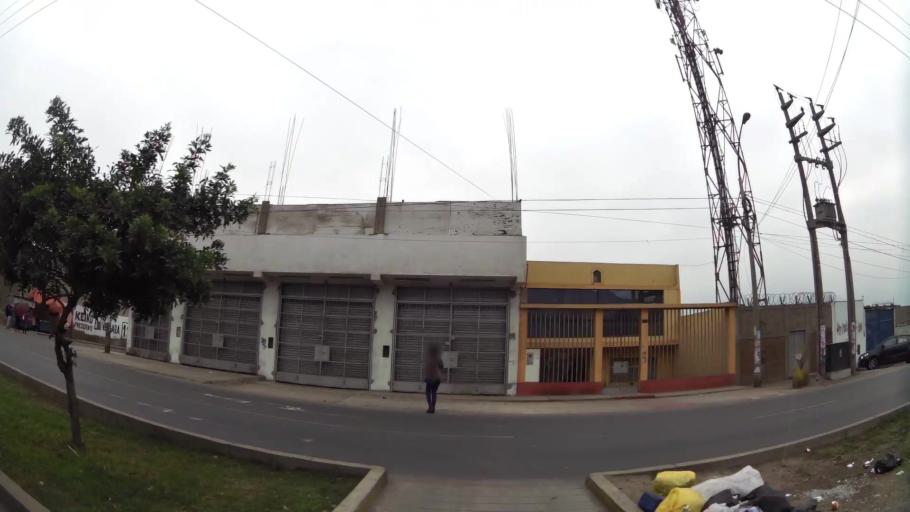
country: PE
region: Lima
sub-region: Lima
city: Independencia
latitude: -11.9772
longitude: -76.9917
